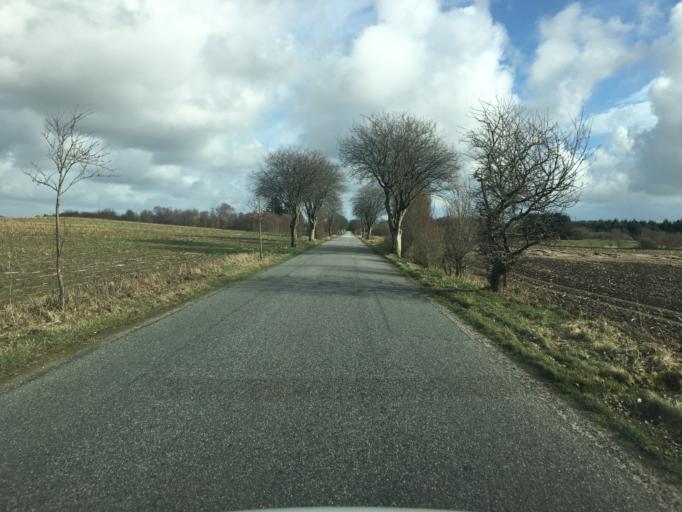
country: DK
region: South Denmark
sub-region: Aabenraa Kommune
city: Krusa
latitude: 54.9016
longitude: 9.3959
